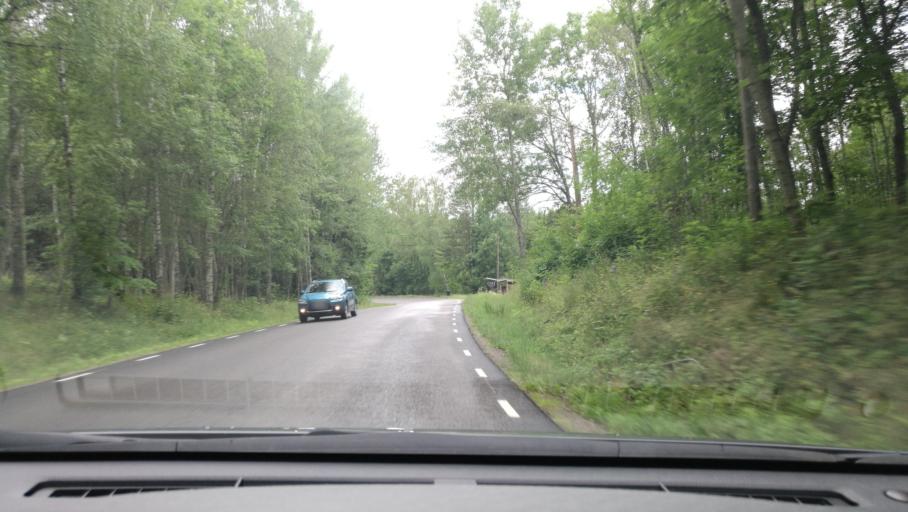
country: SE
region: OEstergoetland
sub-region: Norrkopings Kommun
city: Svartinge
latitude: 58.8194
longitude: 16.0150
